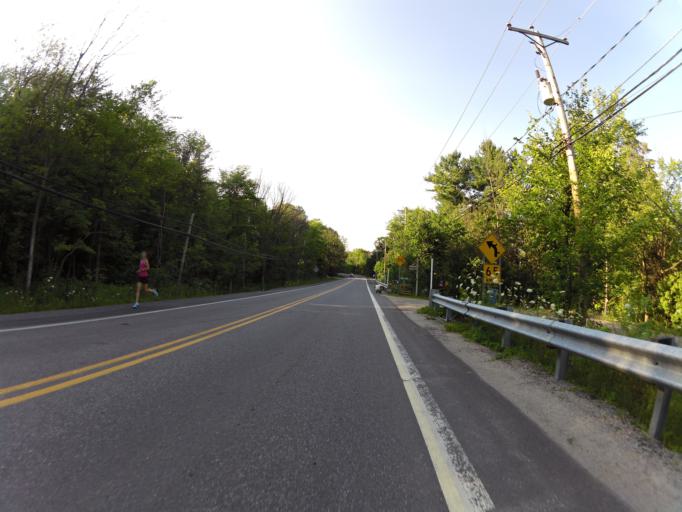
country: CA
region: Quebec
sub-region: Outaouais
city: Wakefield
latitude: 45.5487
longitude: -75.8212
